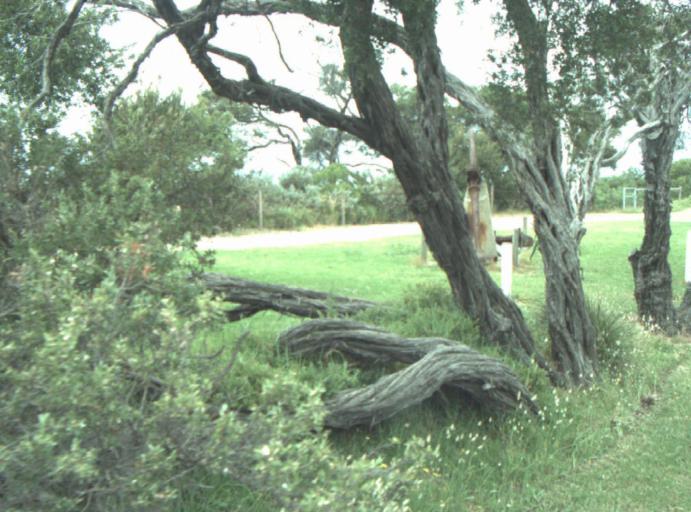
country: AU
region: Victoria
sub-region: Queenscliffe
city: Queenscliff
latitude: -38.1378
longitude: 144.7107
